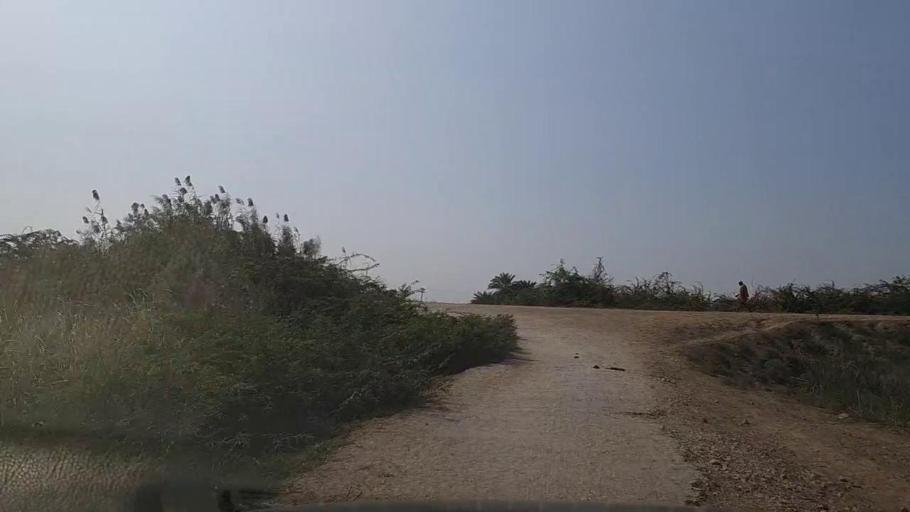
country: PK
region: Sindh
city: Chuhar Jamali
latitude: 24.5423
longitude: 67.9128
